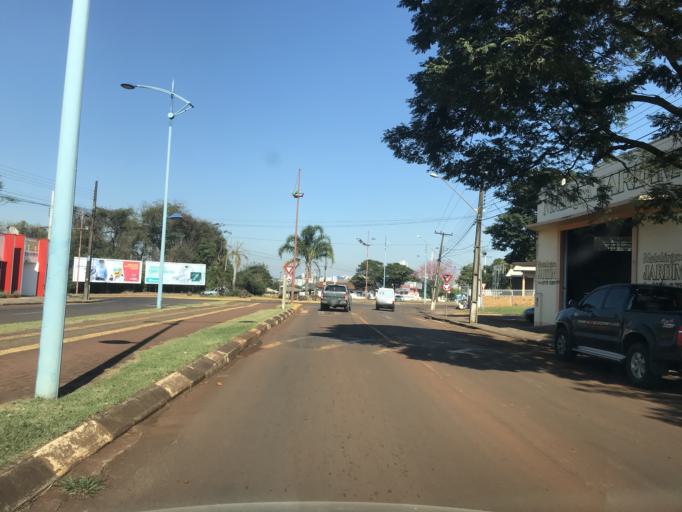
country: BR
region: Parana
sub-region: Toledo
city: Toledo
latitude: -24.7249
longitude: -53.7239
